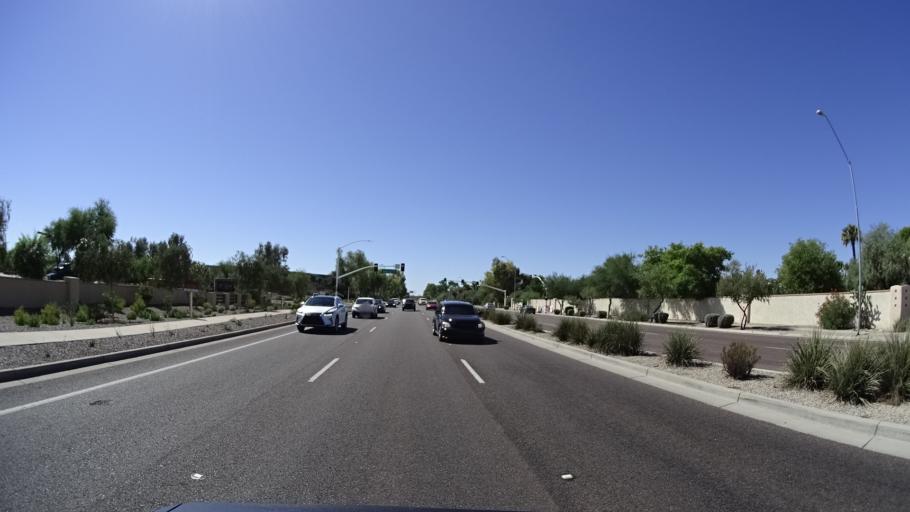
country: US
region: Arizona
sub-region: Maricopa County
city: Paradise Valley
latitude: 33.5646
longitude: -111.9260
